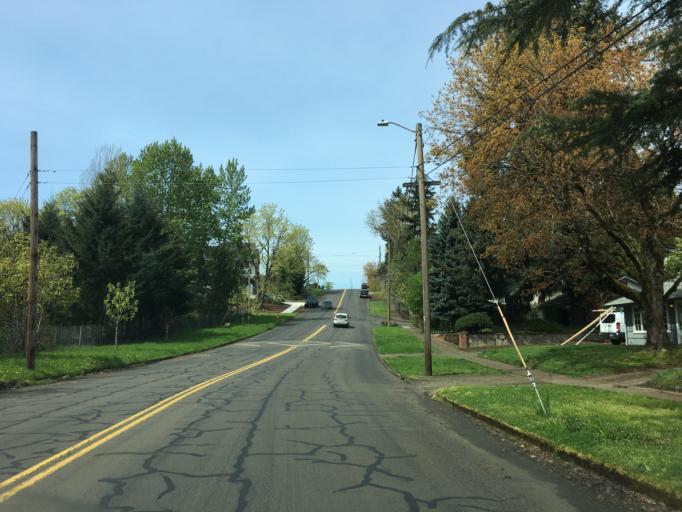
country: US
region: Oregon
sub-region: Multnomah County
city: Lents
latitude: 45.5426
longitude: -122.5716
